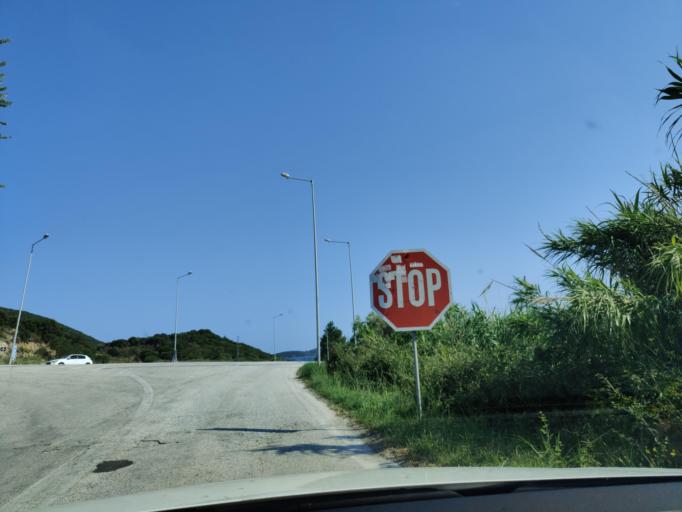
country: GR
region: East Macedonia and Thrace
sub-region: Nomos Kavalas
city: Nea Iraklitsa
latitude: 40.8546
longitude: 24.3137
